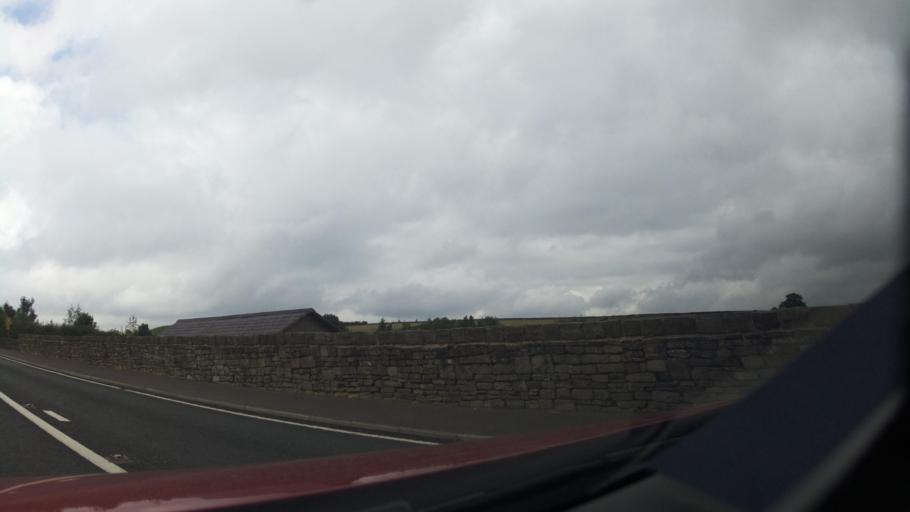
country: GB
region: England
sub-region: Kirklees
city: Kirkburton
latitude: 53.5759
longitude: -1.7236
